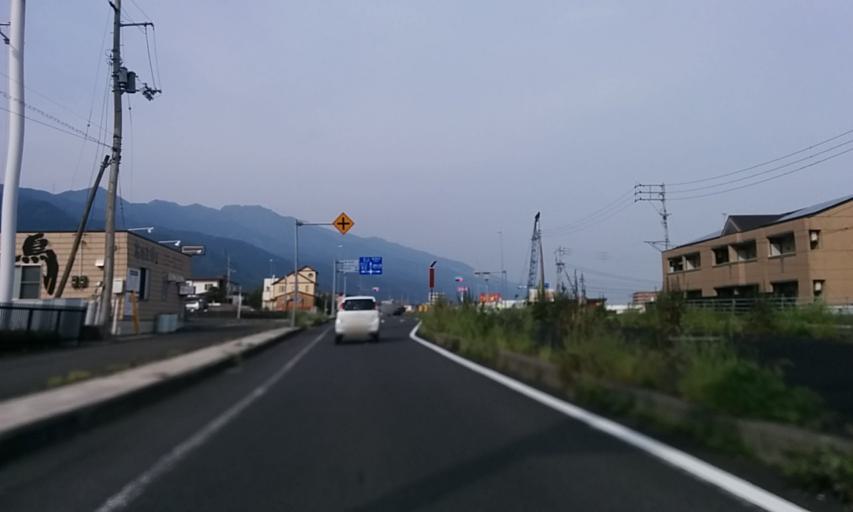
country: JP
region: Ehime
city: Kawanoecho
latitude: 33.9752
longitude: 133.5441
